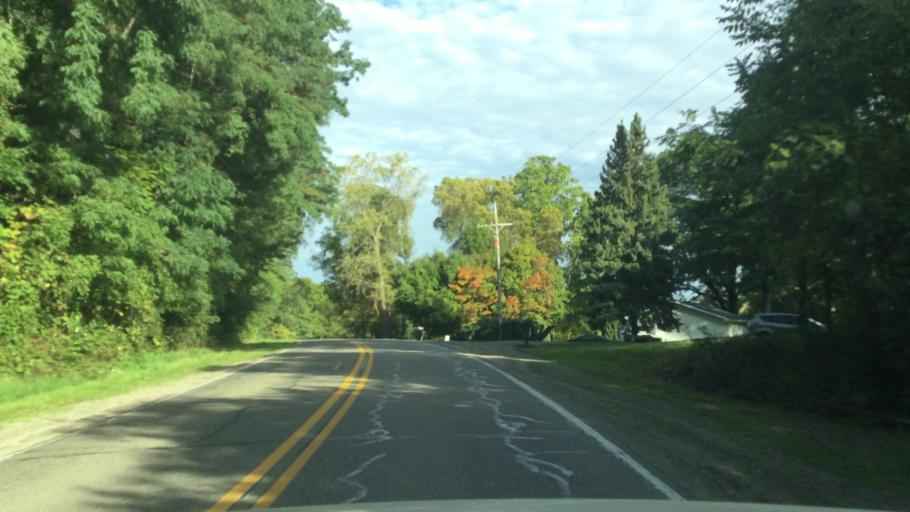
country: US
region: Michigan
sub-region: Livingston County
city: Howell
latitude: 42.5624
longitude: -83.8906
